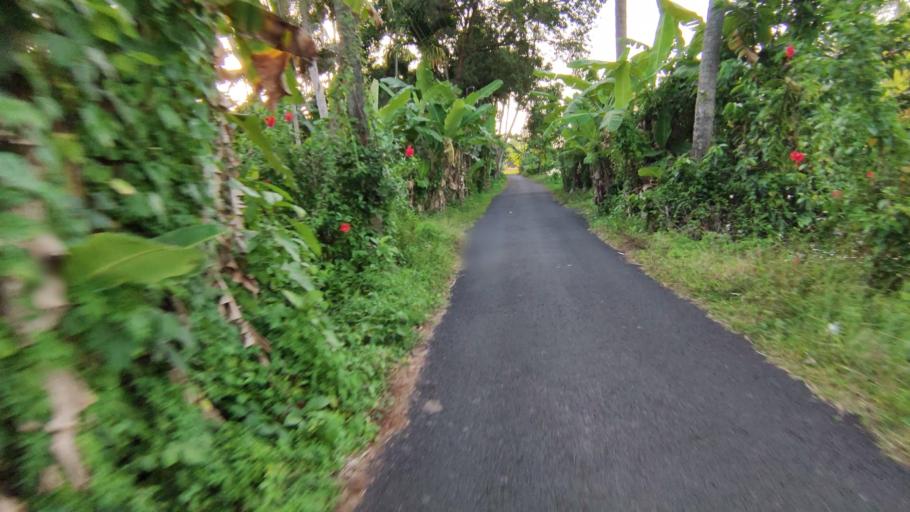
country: IN
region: Kerala
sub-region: Kottayam
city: Kottayam
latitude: 9.5773
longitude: 76.4435
